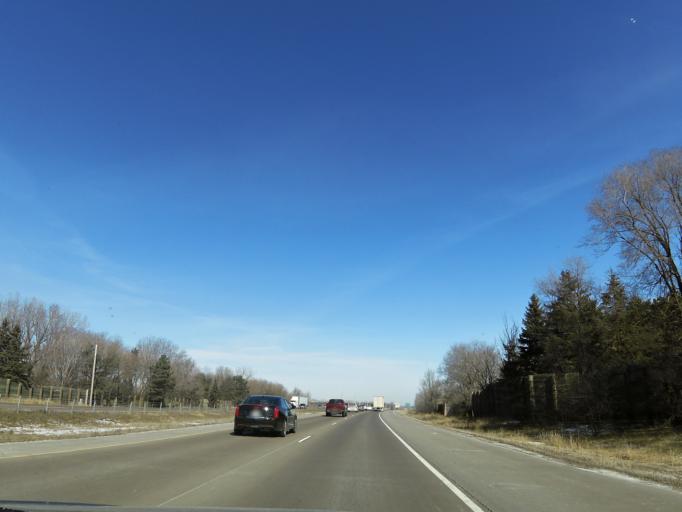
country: US
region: Minnesota
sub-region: Washington County
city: Oakdale
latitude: 44.9903
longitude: -92.9606
